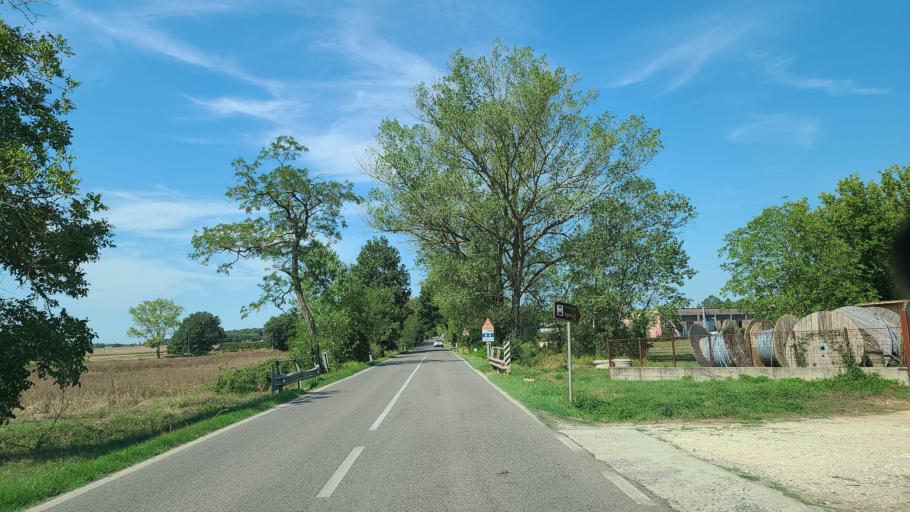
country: IT
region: Tuscany
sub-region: Provincia di Siena
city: Castellina Scalo
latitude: 43.3931
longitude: 11.1987
